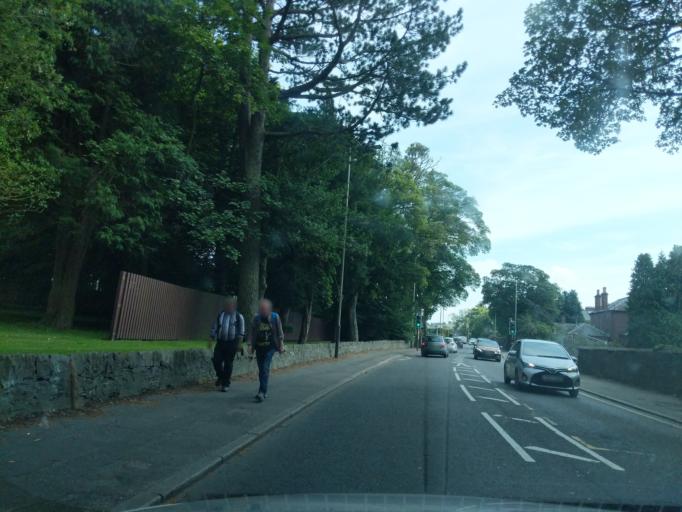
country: GB
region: Scotland
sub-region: Dundee City
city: Dundee
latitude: 56.4781
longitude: -3.0181
